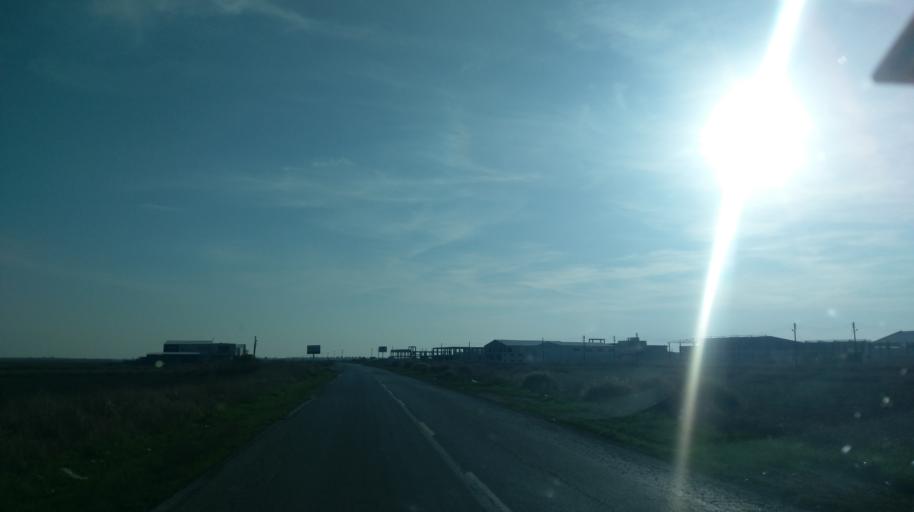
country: CY
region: Ammochostos
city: Acheritou
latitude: 35.1360
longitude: 33.8725
